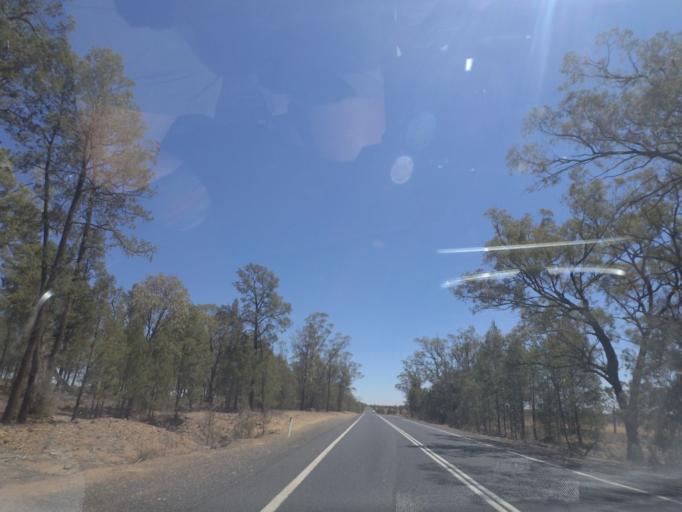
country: AU
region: New South Wales
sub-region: Gilgandra
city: Gilgandra
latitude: -31.4863
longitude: 148.8790
